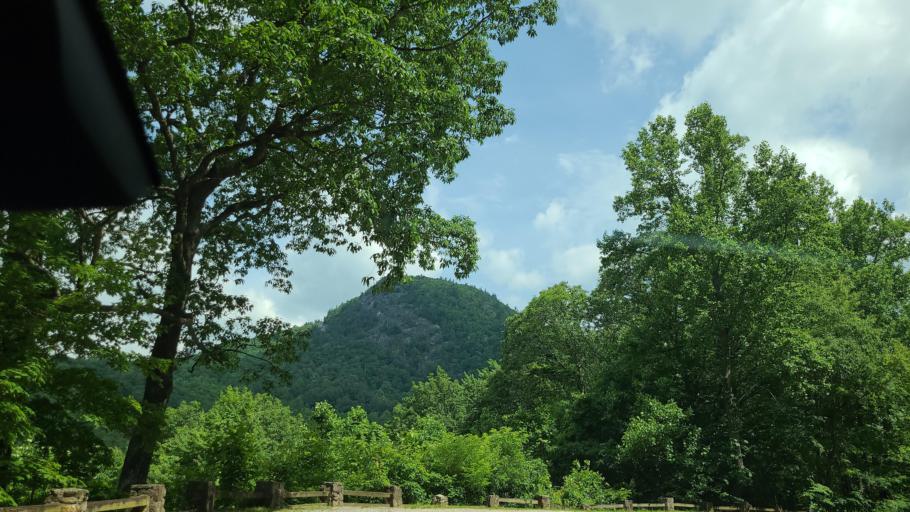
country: US
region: Georgia
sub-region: Rabun County
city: Mountain City
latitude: 35.0238
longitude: -83.1865
